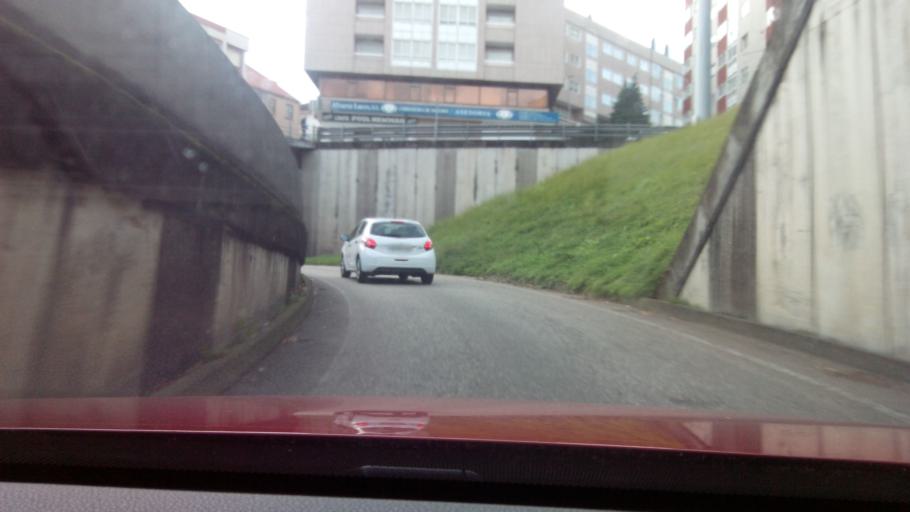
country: ES
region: Galicia
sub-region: Provincia de Pontevedra
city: Vigo
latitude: 42.2248
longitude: -8.7088
